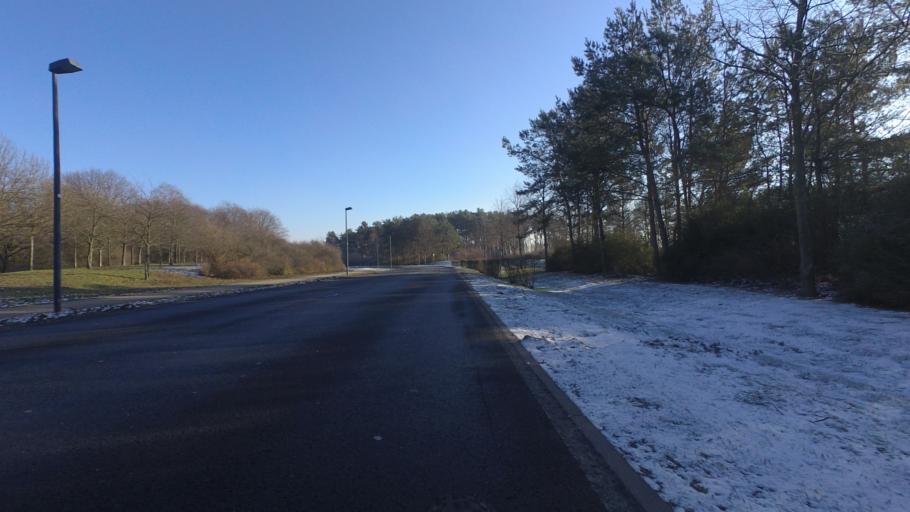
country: DE
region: Brandenburg
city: Ludwigsfelde
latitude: 52.3098
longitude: 13.3009
